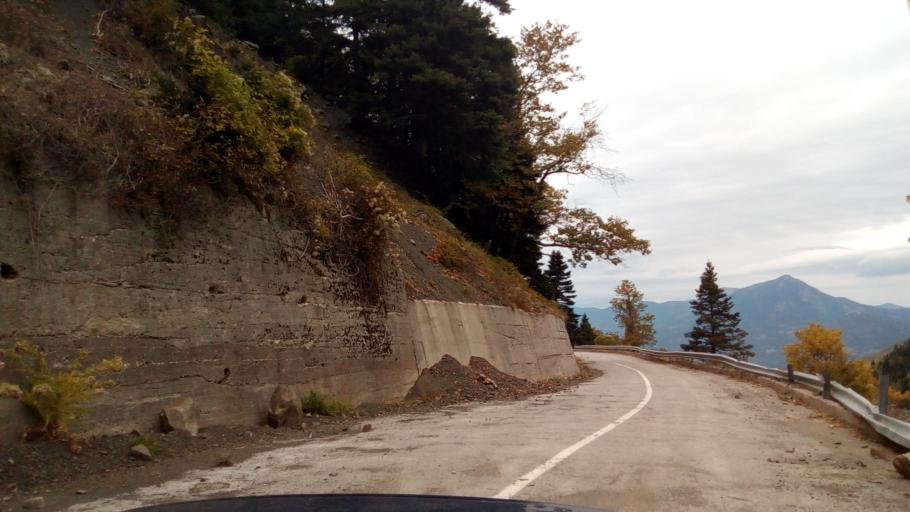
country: GR
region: Central Greece
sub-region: Nomos Fokidos
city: Lidoriki
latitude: 38.4740
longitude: 22.0717
